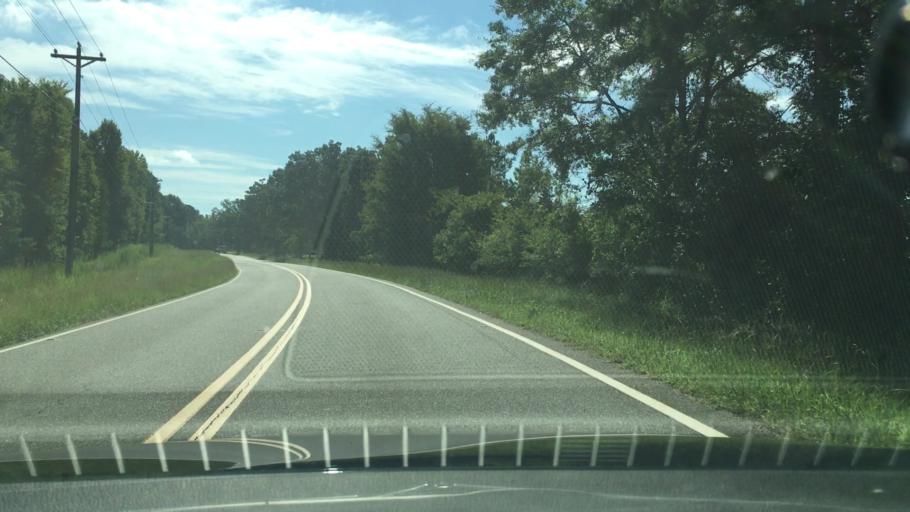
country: US
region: Georgia
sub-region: Putnam County
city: Jefferson
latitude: 33.4436
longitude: -83.2899
